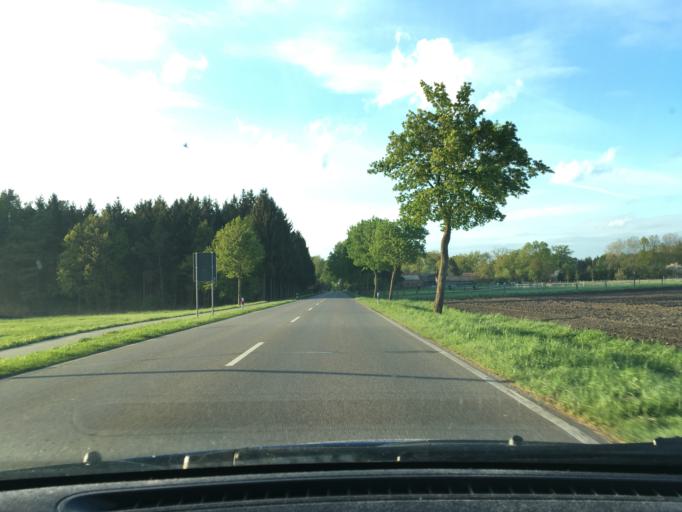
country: DE
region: Lower Saxony
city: Wietzendorf
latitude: 52.9379
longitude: 9.9829
